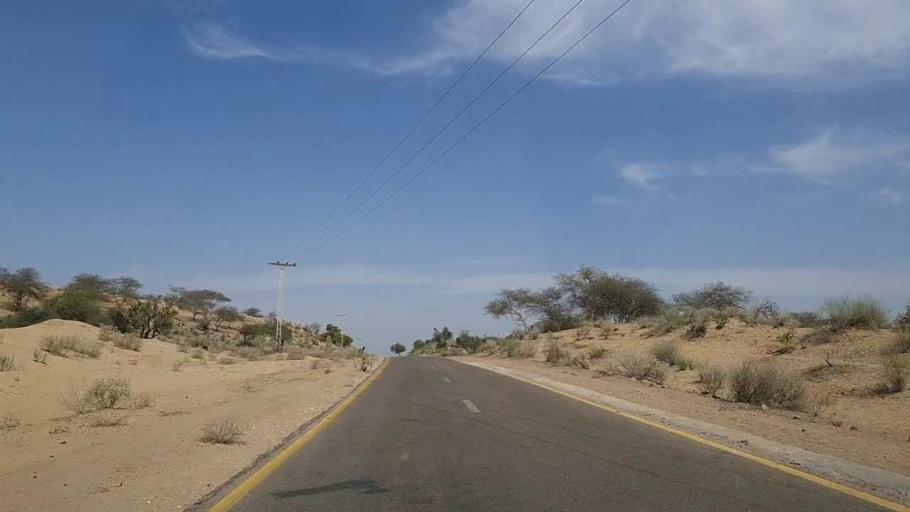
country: PK
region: Sindh
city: Mithi
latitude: 24.8326
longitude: 69.8312
